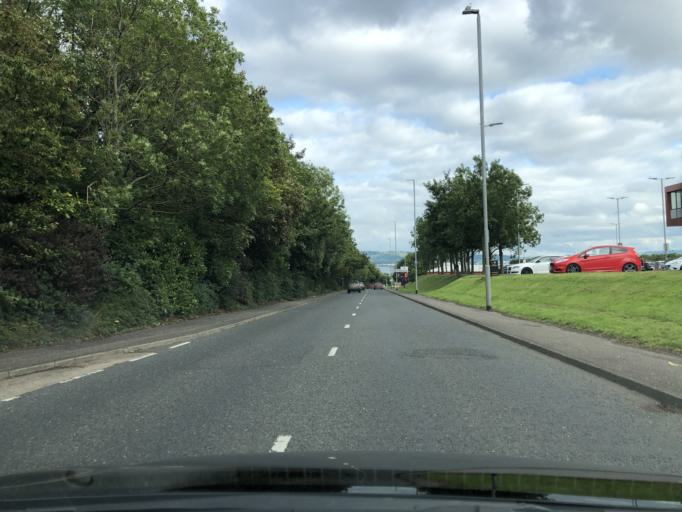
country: GB
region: Northern Ireland
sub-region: Newtownabbey District
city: Newtownabbey
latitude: 54.6564
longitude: -5.9168
